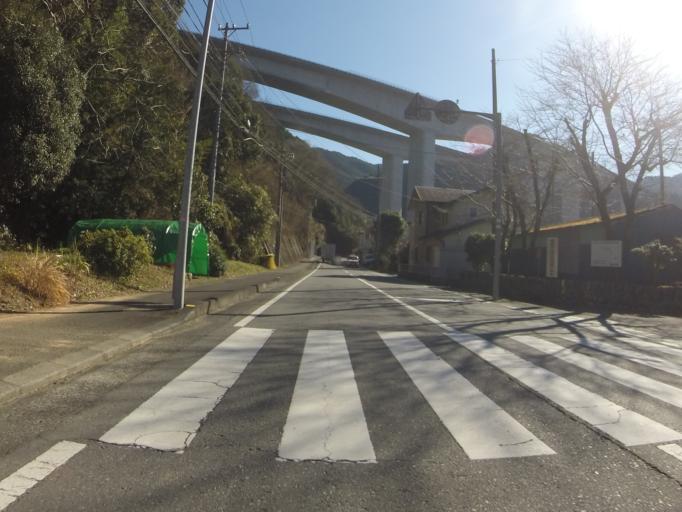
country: JP
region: Shizuoka
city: Shizuoka-shi
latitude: 35.1087
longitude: 138.4813
